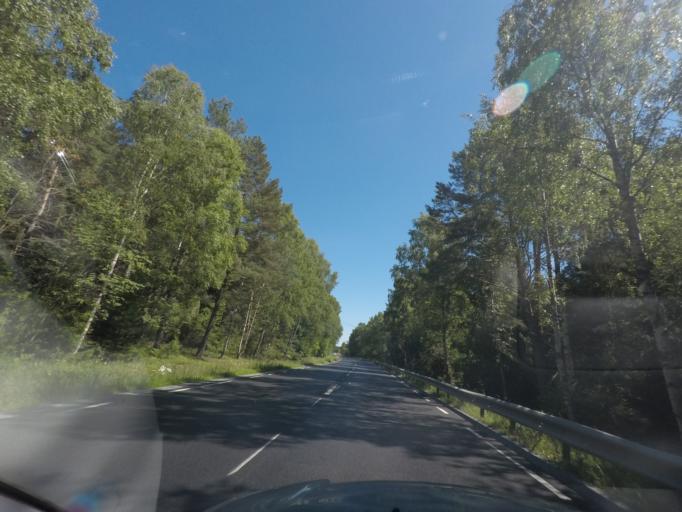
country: SE
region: Uppsala
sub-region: Habo Kommun
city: Balsta
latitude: 59.6347
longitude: 17.5839
